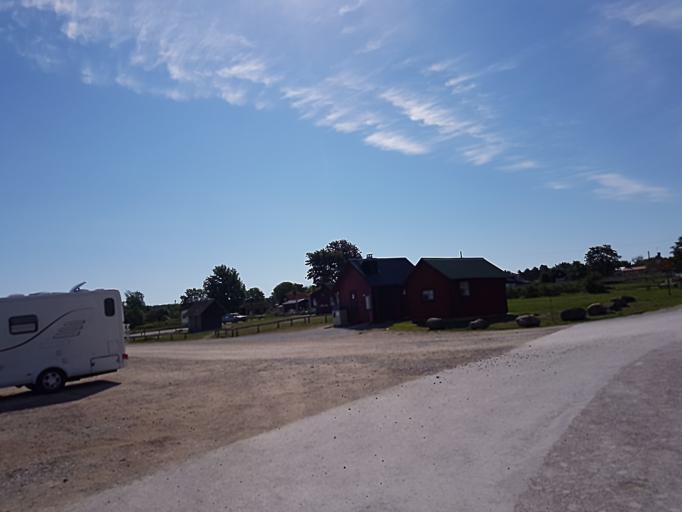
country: SE
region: Gotland
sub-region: Gotland
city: Visby
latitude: 57.8256
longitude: 18.5131
